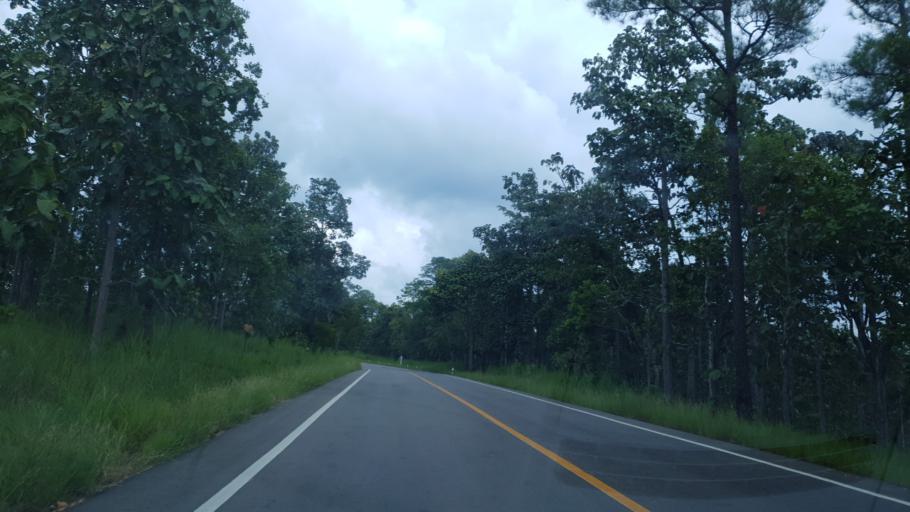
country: TH
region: Mae Hong Son
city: Khun Yuam
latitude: 18.7585
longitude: 97.9312
